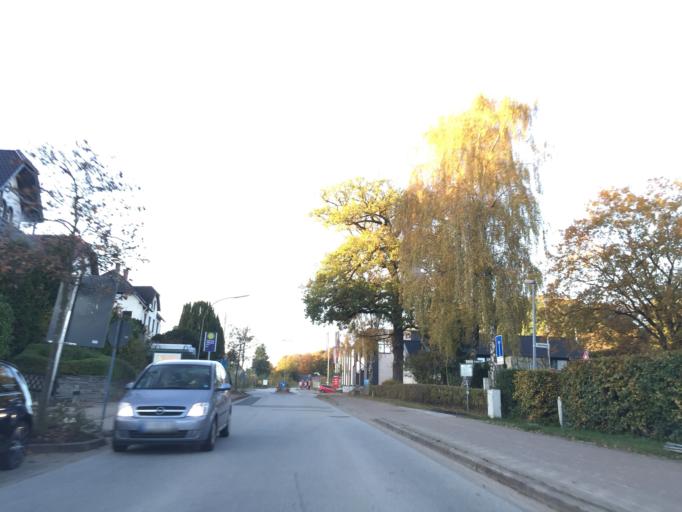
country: DK
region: South Denmark
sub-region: Aabenraa Kommune
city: Krusa
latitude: 54.8300
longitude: 9.4161
